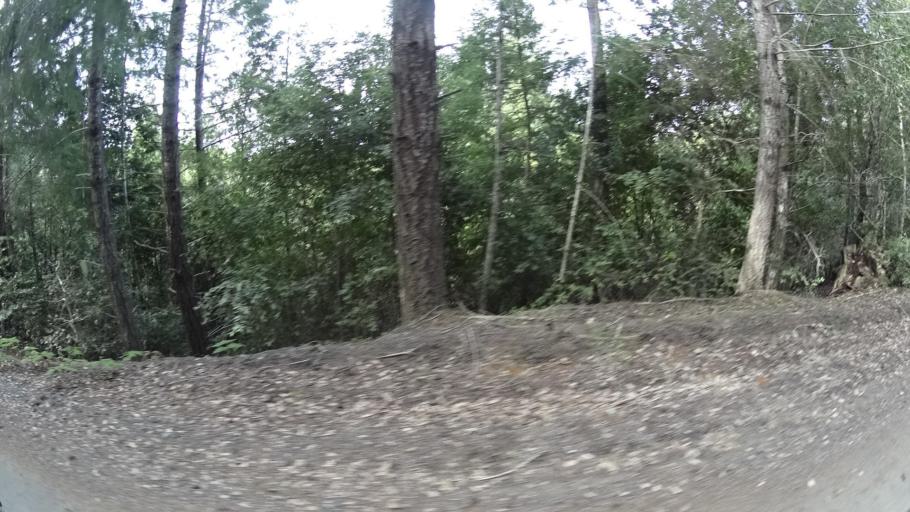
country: US
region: California
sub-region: Humboldt County
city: Redway
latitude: 40.0338
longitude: -123.8376
